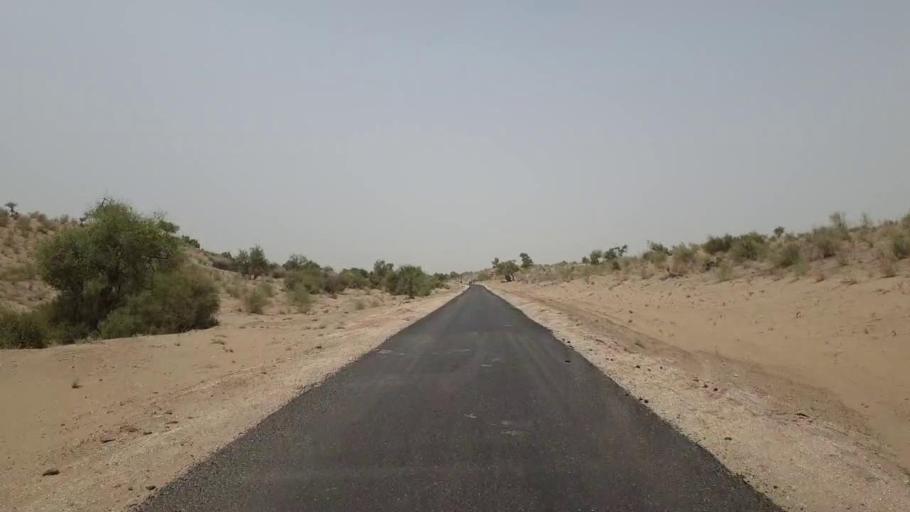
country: PK
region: Sindh
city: Islamkot
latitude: 24.8020
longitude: 70.5534
